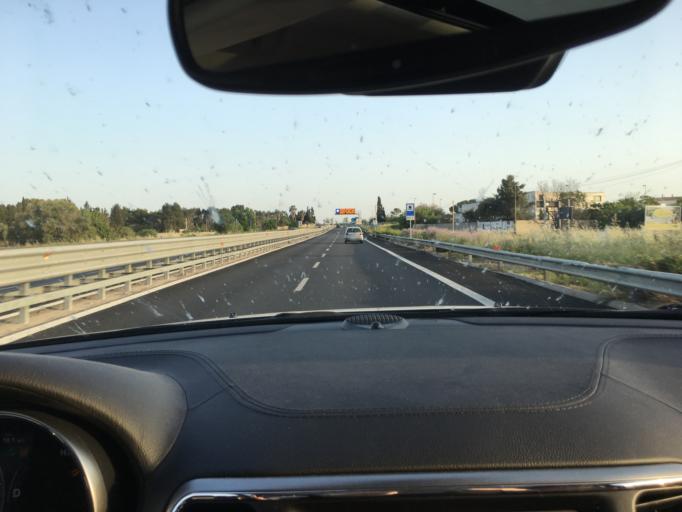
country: IT
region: Apulia
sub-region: Provincia di Lecce
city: San Pietro in Lama
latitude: 40.2958
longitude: 18.1323
